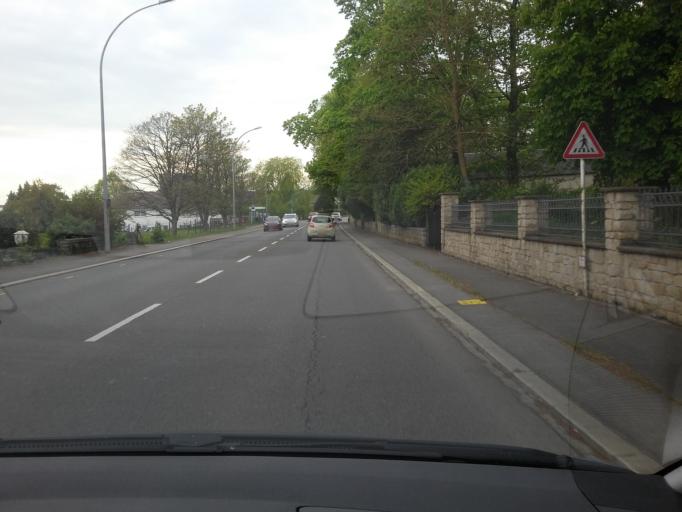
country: LU
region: Luxembourg
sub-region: Canton de Capellen
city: Dippach
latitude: 49.5877
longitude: 5.9887
